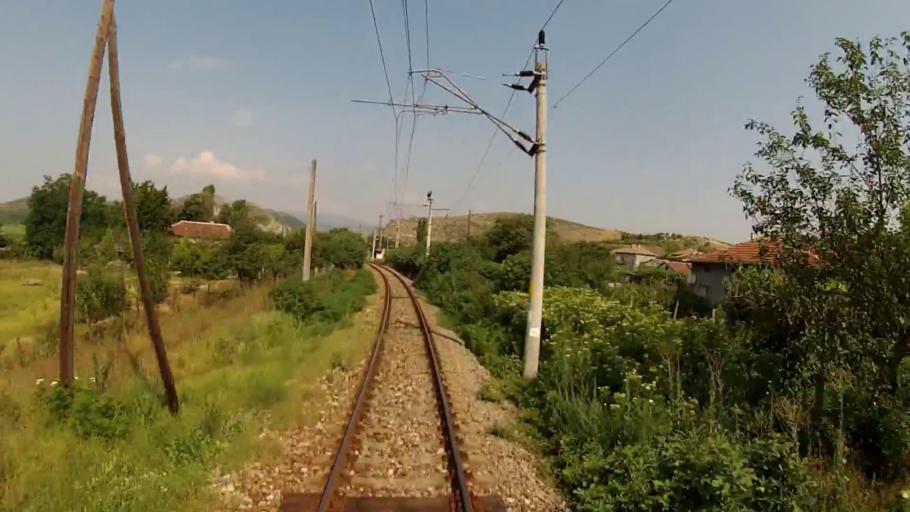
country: BG
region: Blagoevgrad
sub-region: Obshtina Petrich
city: Petrich
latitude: 41.4518
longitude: 23.2882
